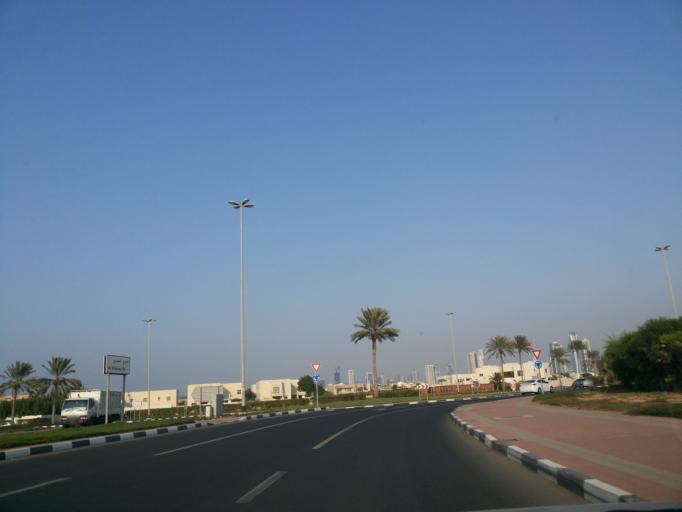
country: AE
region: Ash Shariqah
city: Sharjah
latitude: 25.3064
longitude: 55.3408
